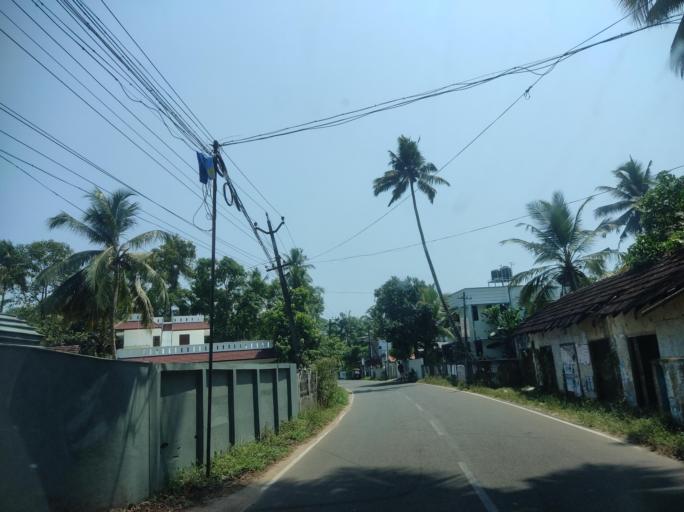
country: IN
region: Kerala
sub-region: Alappuzha
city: Kutiatodu
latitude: 9.8043
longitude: 76.3011
